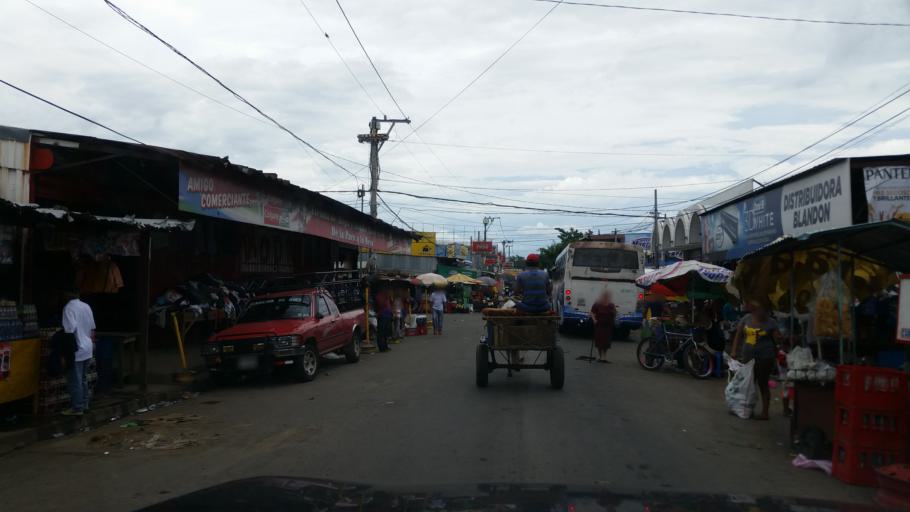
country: NI
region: Managua
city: Managua
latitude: 12.1451
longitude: -86.2633
